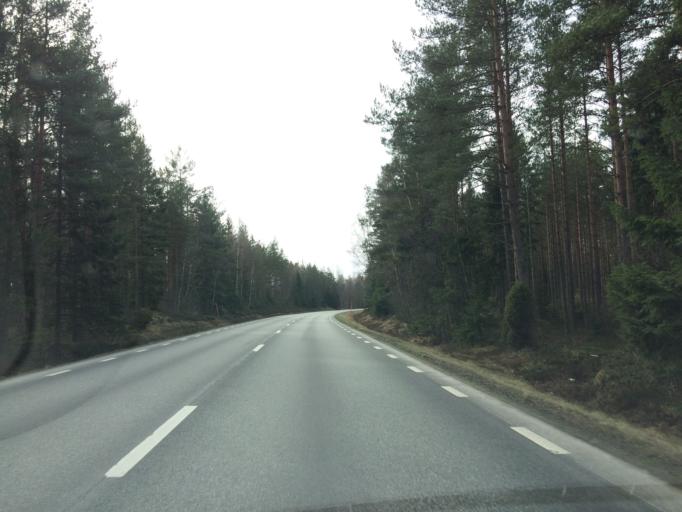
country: SE
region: Skane
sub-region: Osby Kommun
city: Lonsboda
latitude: 56.3855
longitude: 14.2739
